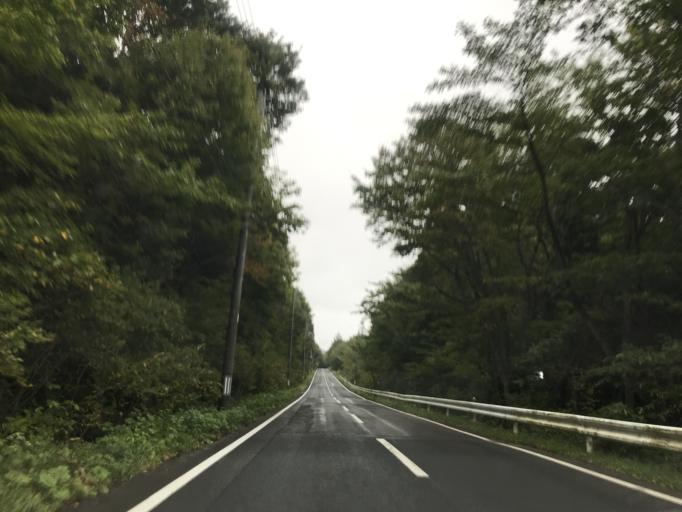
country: JP
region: Iwate
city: Ichinoseki
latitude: 39.0105
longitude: 140.8904
